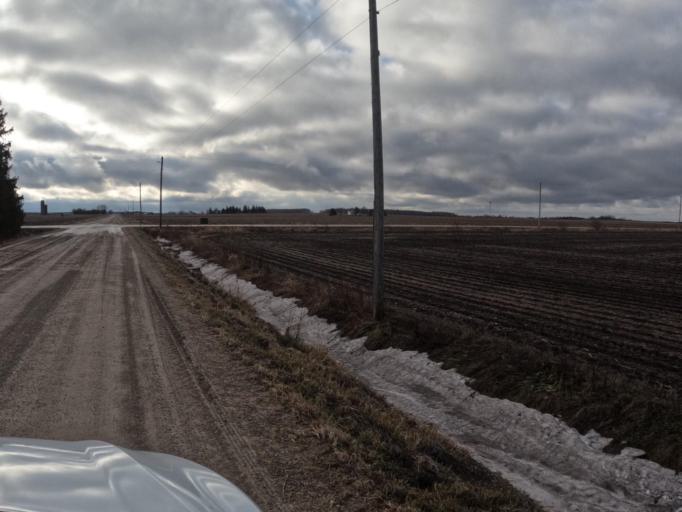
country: CA
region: Ontario
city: Shelburne
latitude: 43.8904
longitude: -80.3602
